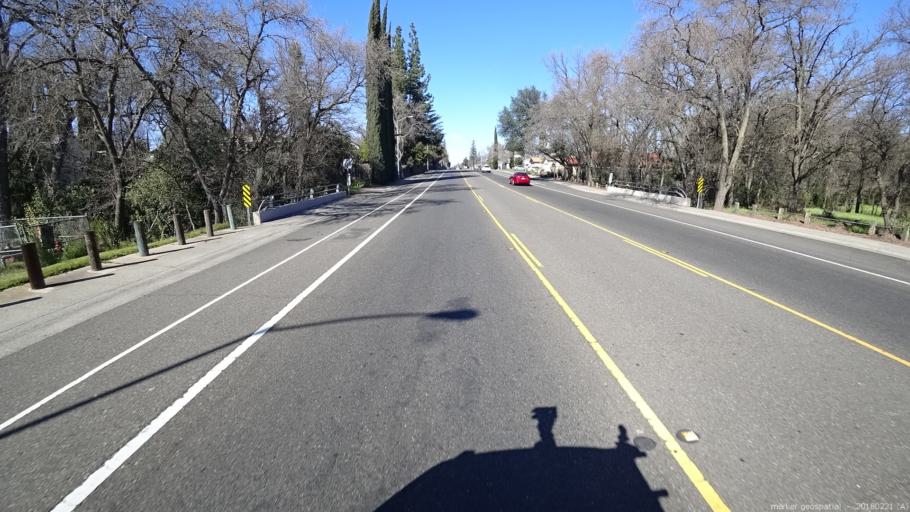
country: US
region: California
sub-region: Sacramento County
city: Citrus Heights
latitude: 38.6884
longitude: -121.2624
